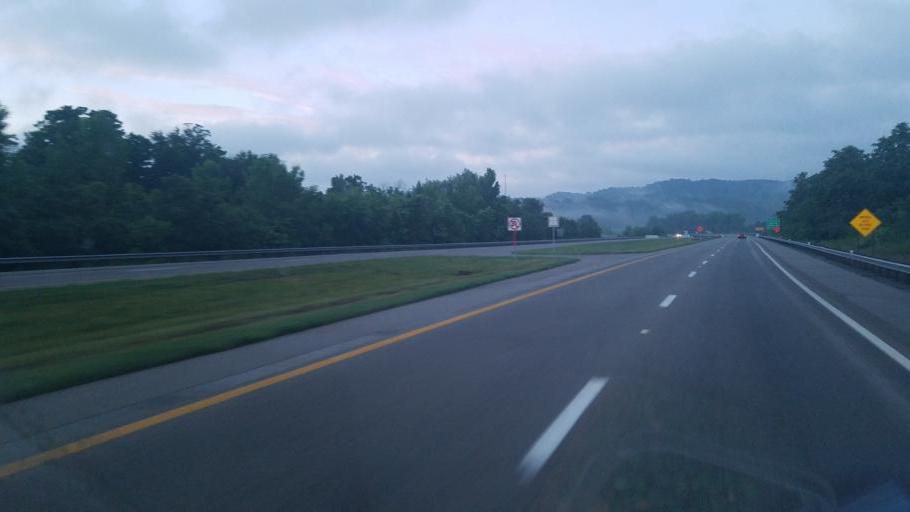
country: US
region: Ohio
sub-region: Pike County
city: Waverly
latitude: 39.2093
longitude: -82.8221
